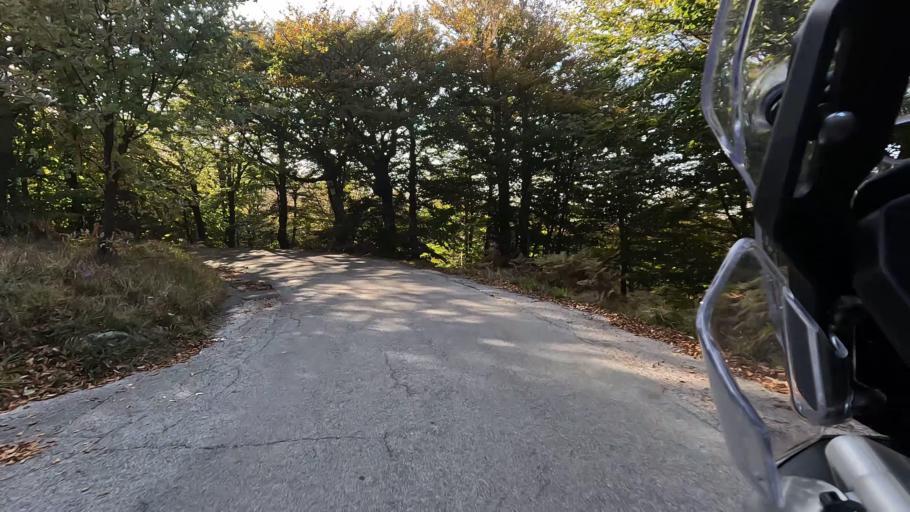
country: IT
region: Liguria
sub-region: Provincia di Savona
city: San Giovanni
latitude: 44.4309
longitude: 8.5446
